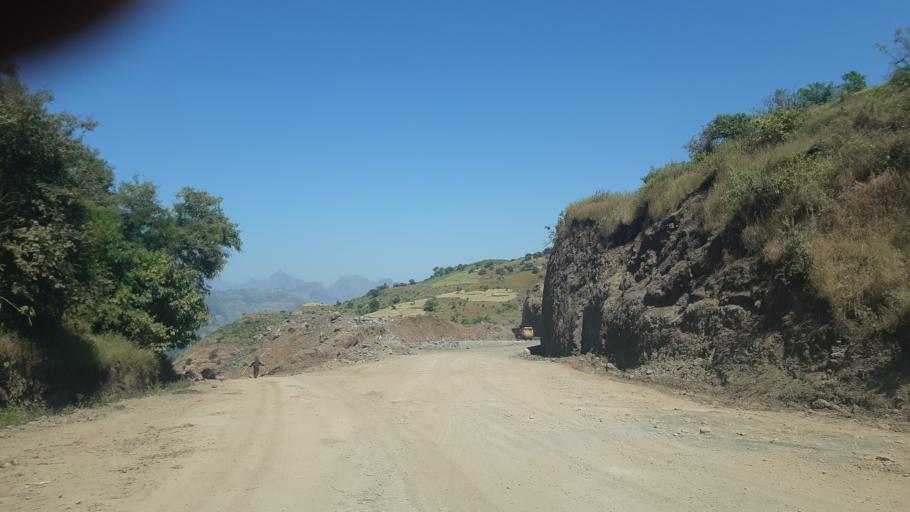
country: ET
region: Amhara
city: Dabat
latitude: 13.1646
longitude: 37.6057
